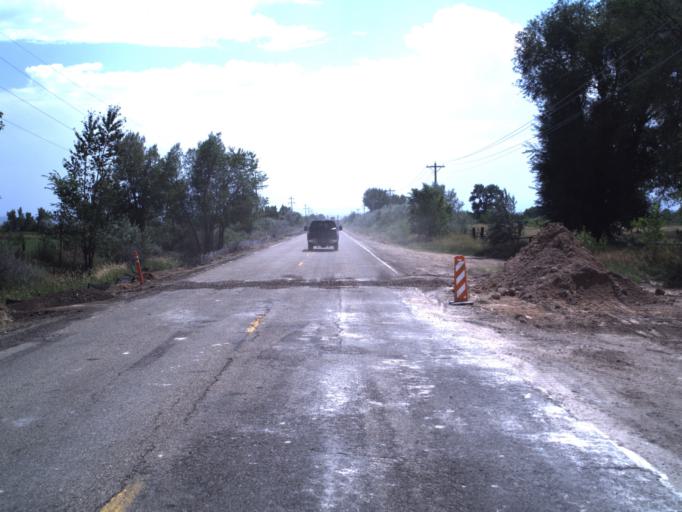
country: US
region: Utah
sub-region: Duchesne County
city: Roosevelt
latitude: 40.3965
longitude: -110.0298
